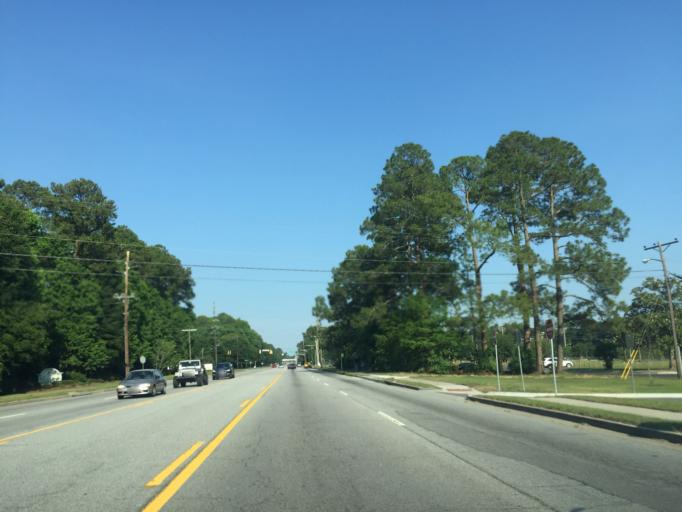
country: US
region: Georgia
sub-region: Chatham County
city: Isle of Hope
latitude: 32.0043
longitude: -81.0927
